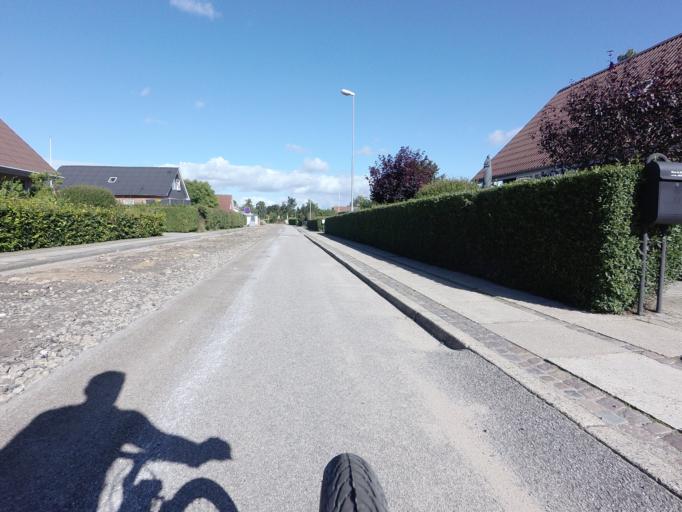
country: DK
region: Central Jutland
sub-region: Skanderborg Kommune
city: Ry
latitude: 55.9649
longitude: 9.7559
